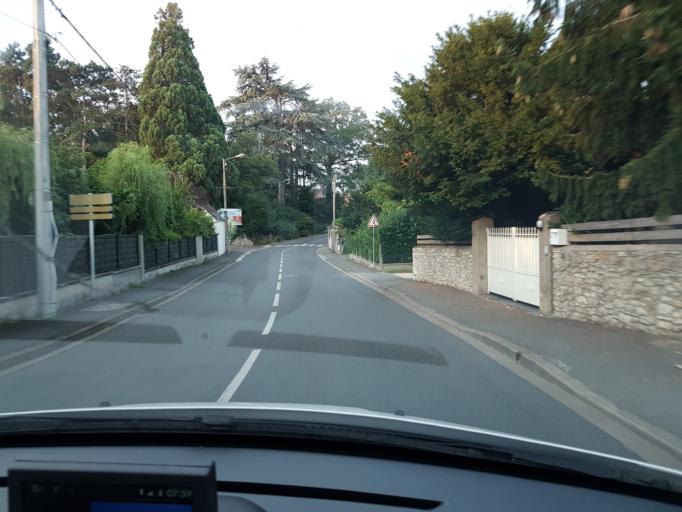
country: FR
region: Centre
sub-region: Departement d'Indre-et-Loire
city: Saint-Avertin
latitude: 47.3608
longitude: 0.7364
